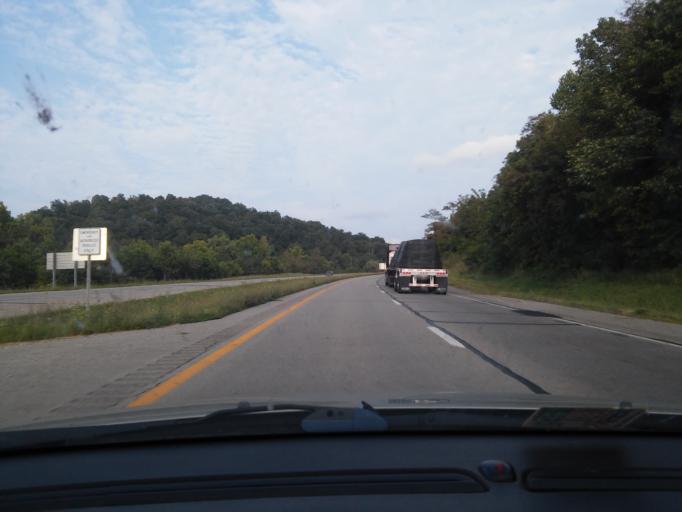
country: US
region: Ohio
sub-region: Gallia County
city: Gallipolis
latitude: 38.8427
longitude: -82.2042
